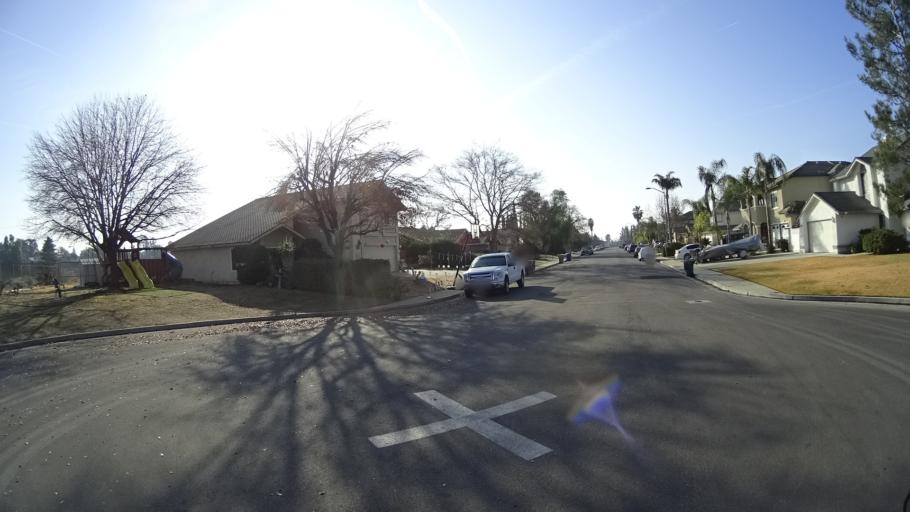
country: US
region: California
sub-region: Kern County
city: Oildale
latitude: 35.4072
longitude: -118.9325
